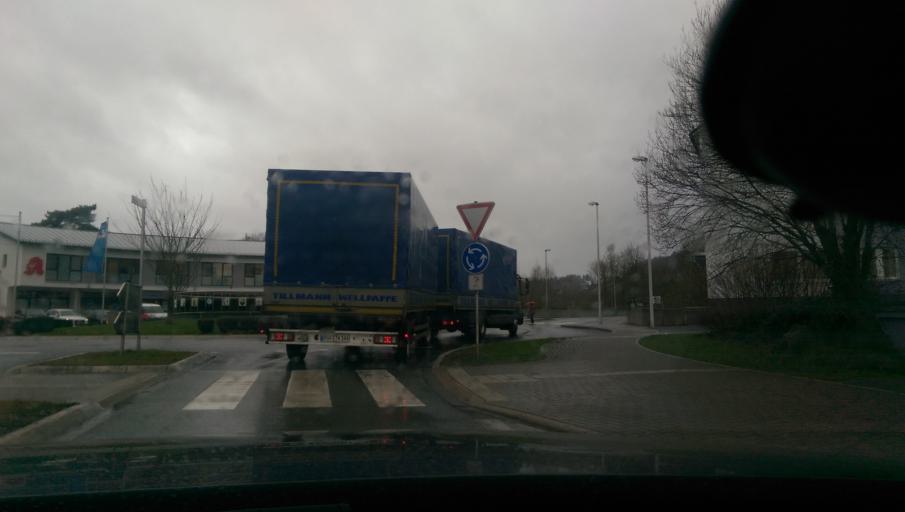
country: DE
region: North Rhine-Westphalia
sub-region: Regierungsbezirk Arnsberg
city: Sundern
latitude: 51.3723
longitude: 7.9795
